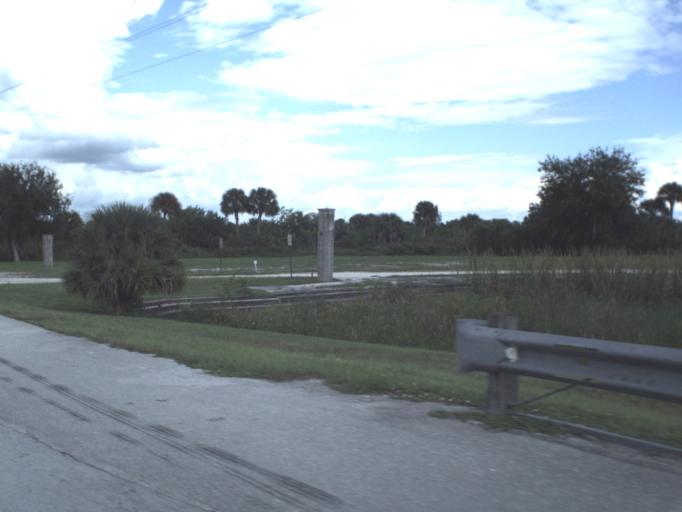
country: US
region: Florida
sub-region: Glades County
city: Moore Haven
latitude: 26.9283
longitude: -81.1223
